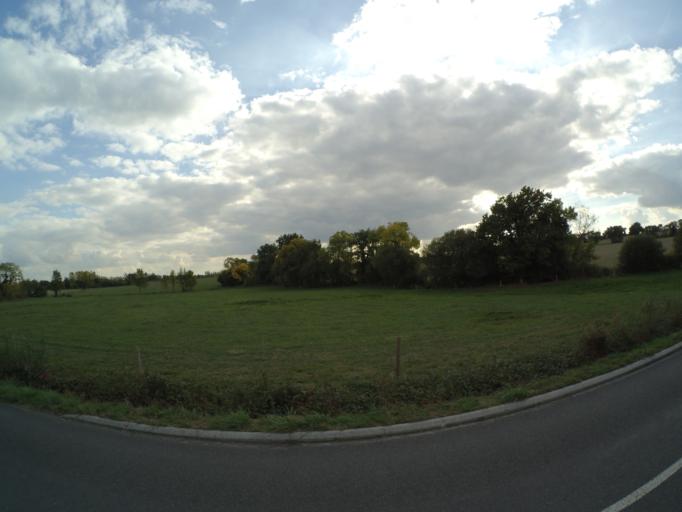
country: FR
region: Pays de la Loire
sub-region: Departement de la Loire-Atlantique
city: Saint-Lumine-de-Clisson
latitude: 47.0583
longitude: -1.3465
